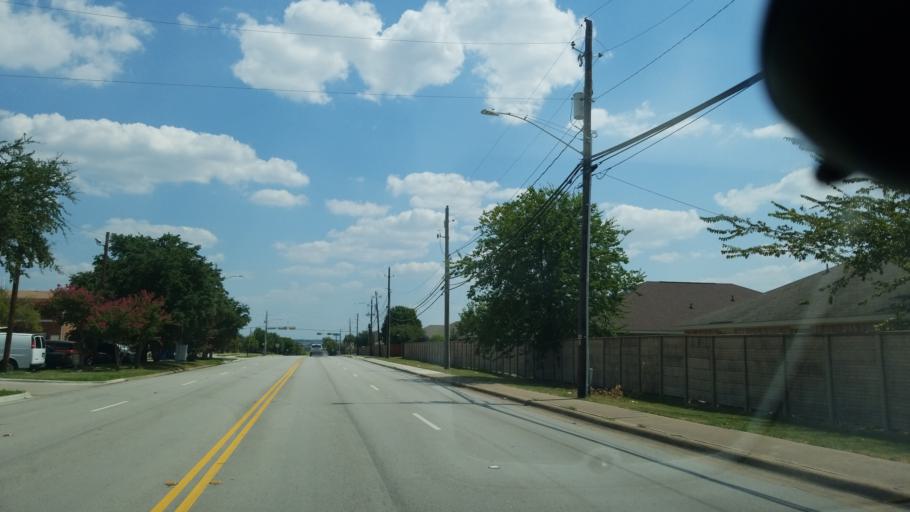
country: US
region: Texas
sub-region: Dallas County
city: Grand Prairie
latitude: 32.6988
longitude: -96.9963
